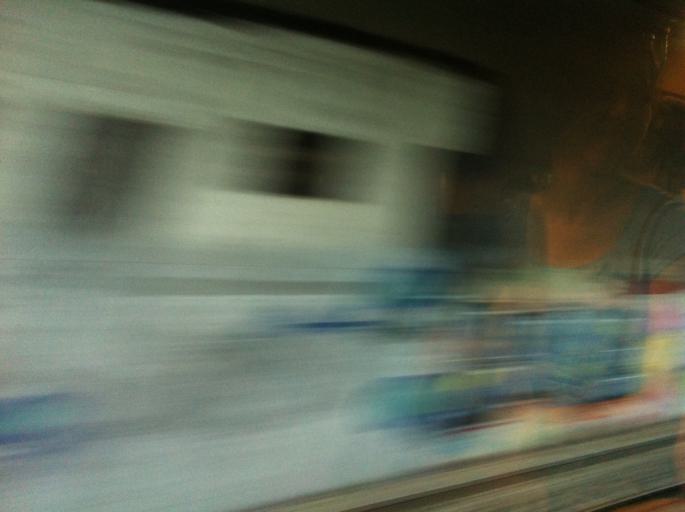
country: DE
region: North Rhine-Westphalia
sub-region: Regierungsbezirk Koln
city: Alfter
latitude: 50.7549
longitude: 7.0468
